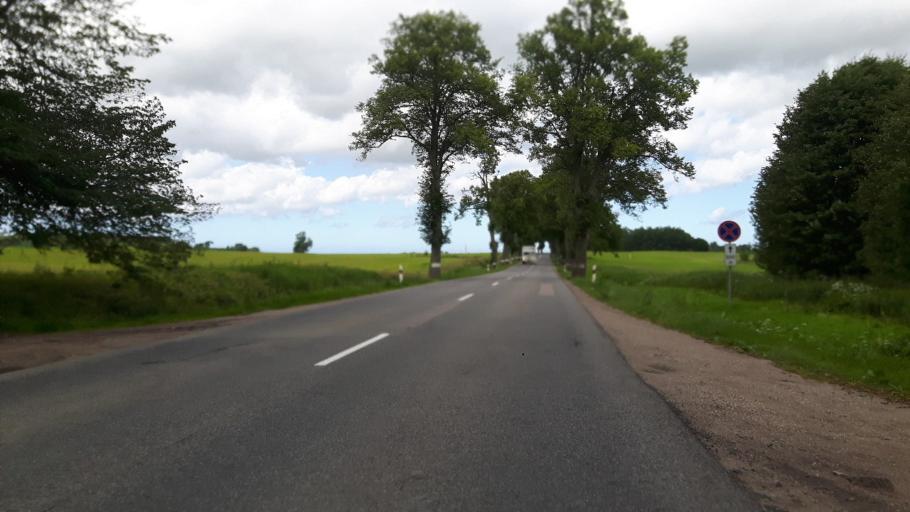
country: RU
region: Kaliningrad
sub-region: Zelenogradskiy Rayon
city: Zelenogradsk
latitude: 54.8705
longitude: 20.4112
